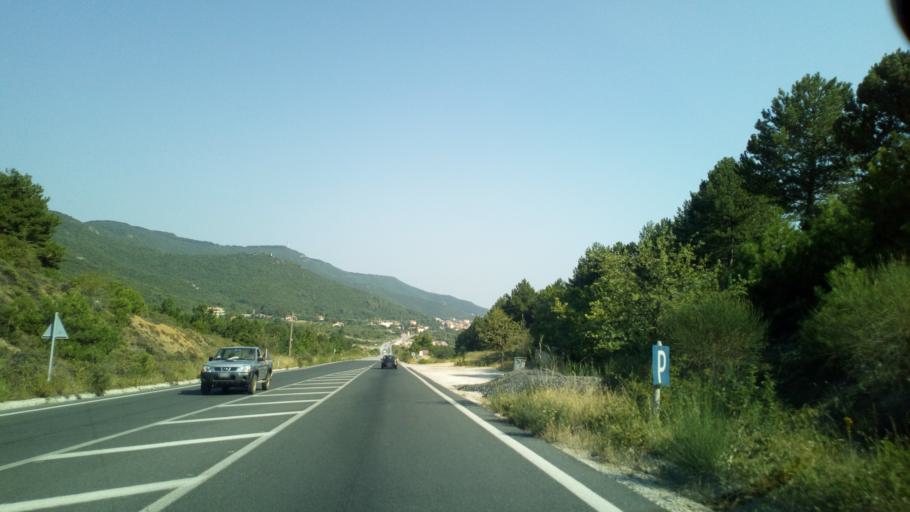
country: GR
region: Central Macedonia
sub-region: Nomos Chalkidikis
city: Polygyros
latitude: 40.3967
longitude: 23.4270
